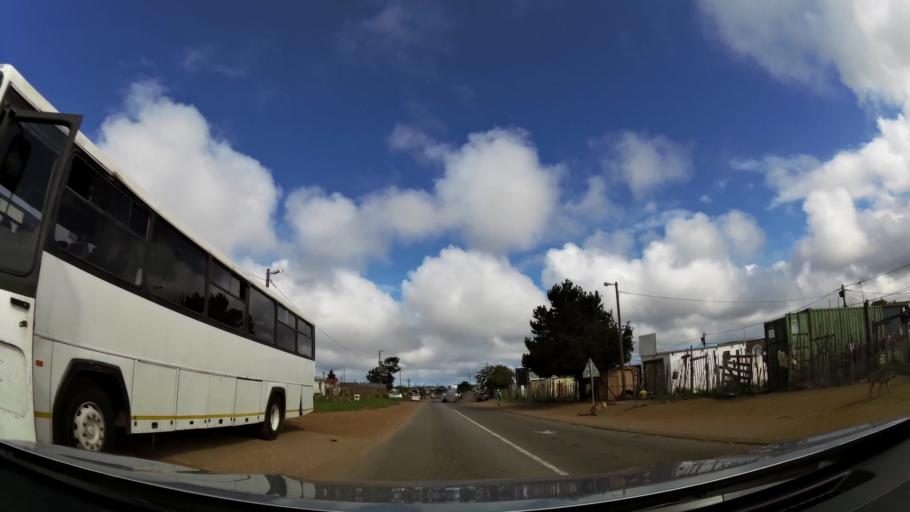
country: ZA
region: Western Cape
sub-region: Eden District Municipality
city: Plettenberg Bay
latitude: -34.0489
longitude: 23.3229
